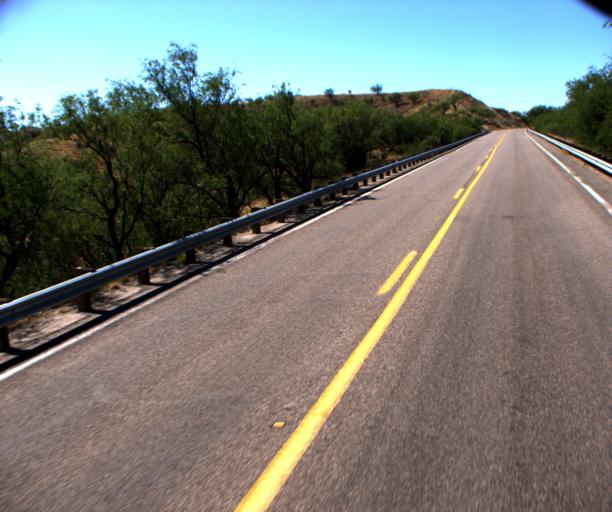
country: US
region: Arizona
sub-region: Santa Cruz County
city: Rio Rico
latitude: 31.4720
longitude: -110.8206
